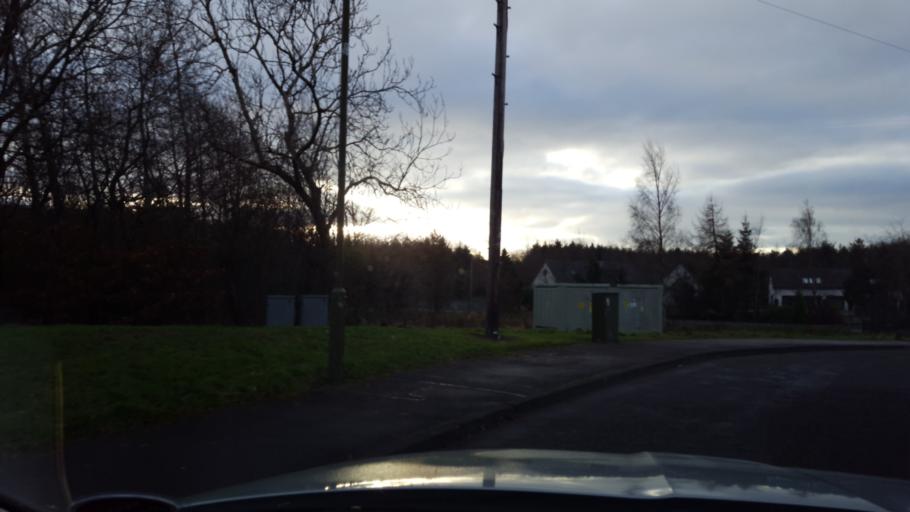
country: GB
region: Scotland
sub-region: West Lothian
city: Livingston
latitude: 55.8577
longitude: -3.5131
